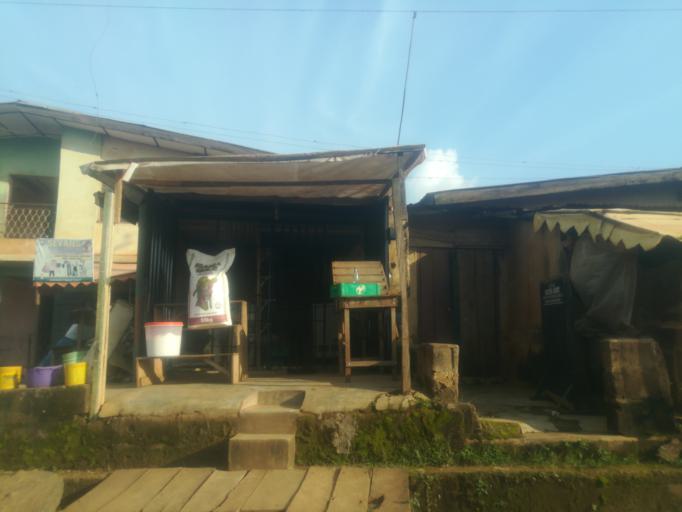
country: NG
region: Oyo
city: Ibadan
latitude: 7.3796
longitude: 3.8169
